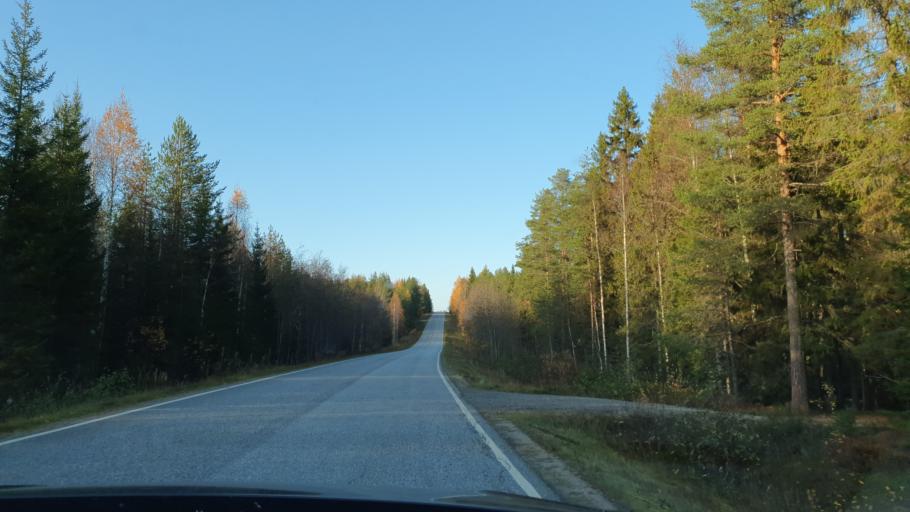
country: FI
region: Kainuu
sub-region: Kehys-Kainuu
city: Kuhmo
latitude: 64.3574
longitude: 29.4890
